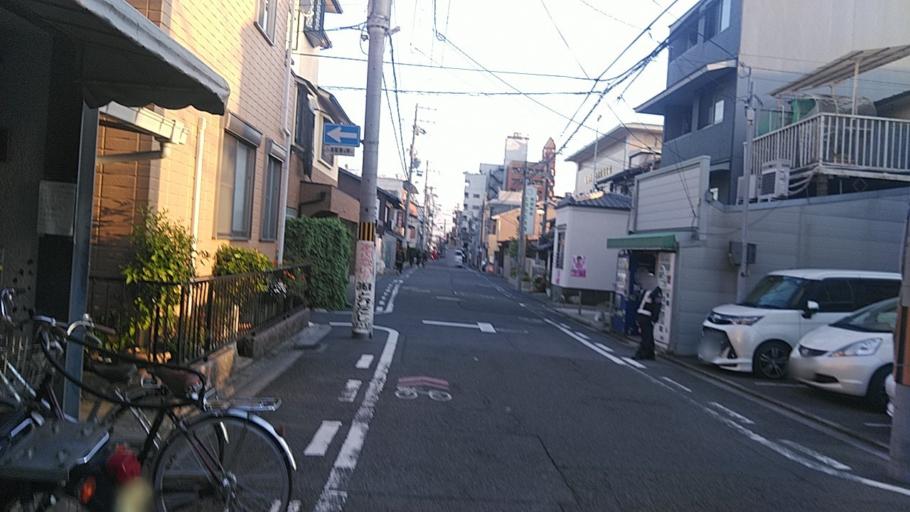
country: JP
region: Kyoto
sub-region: Kyoto-shi
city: Kamigyo-ku
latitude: 35.0307
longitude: 135.7579
